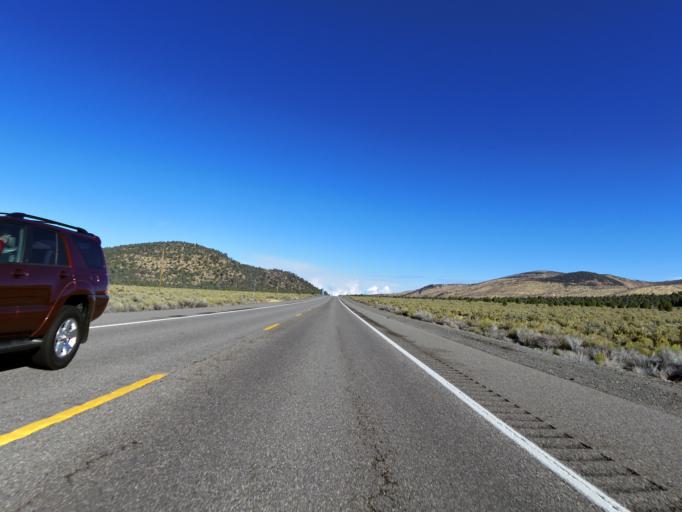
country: US
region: Nevada
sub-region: Douglas County
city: Gardnerville Ranchos
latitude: 38.7967
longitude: -119.6021
